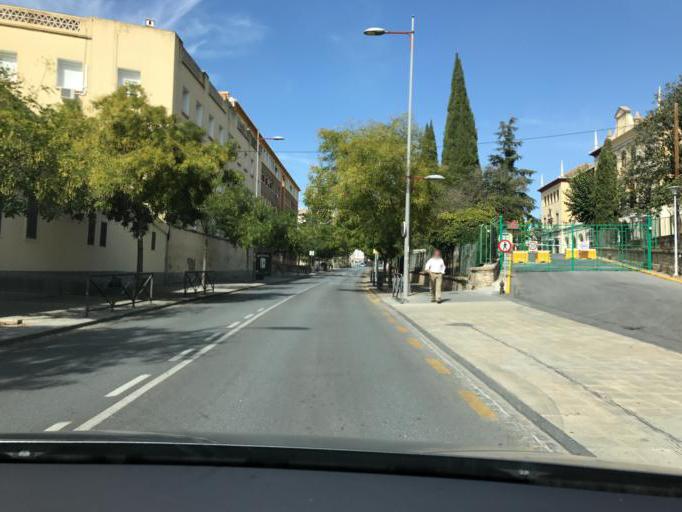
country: ES
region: Andalusia
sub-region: Provincia de Granada
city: Granada
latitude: 37.1924
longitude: -3.6041
